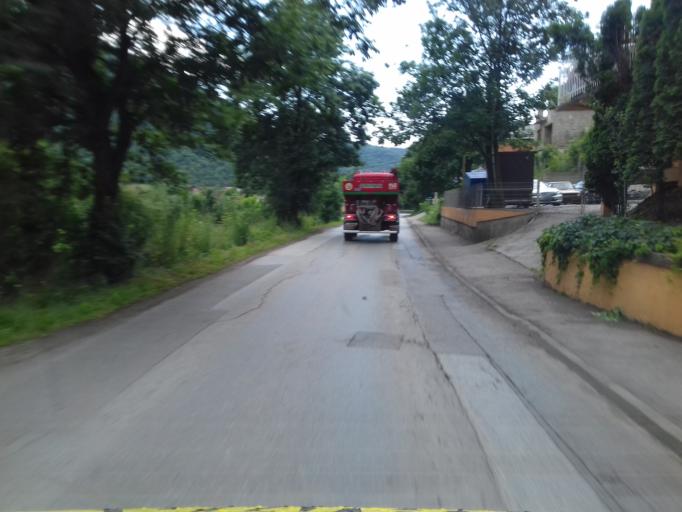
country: BA
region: Federation of Bosnia and Herzegovina
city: Visoko
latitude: 43.9724
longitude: 18.1881
